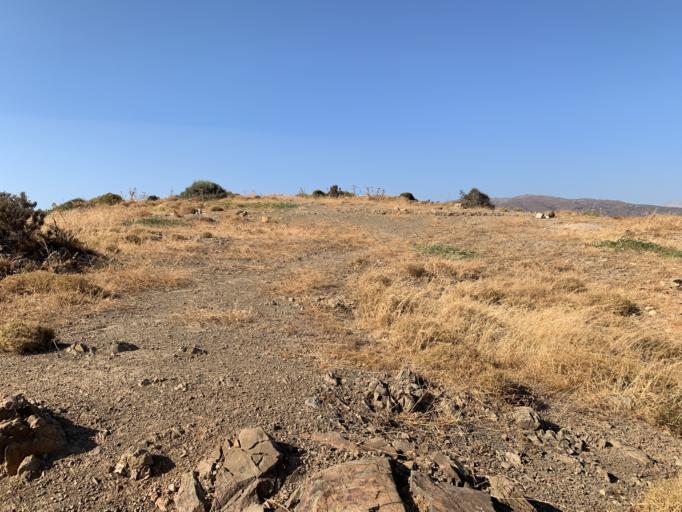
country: GR
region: North Aegean
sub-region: Chios
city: Vrontados
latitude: 38.4869
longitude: 25.8759
